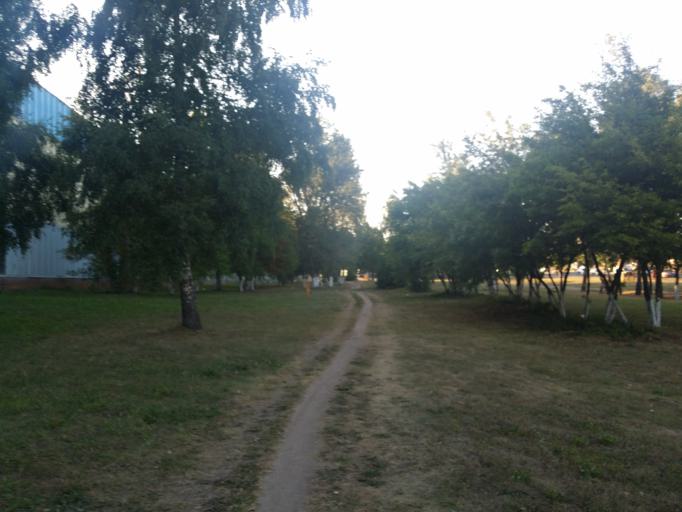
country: BY
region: Minsk
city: Vyaliki Trastsyanets
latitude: 53.8534
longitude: 27.6928
